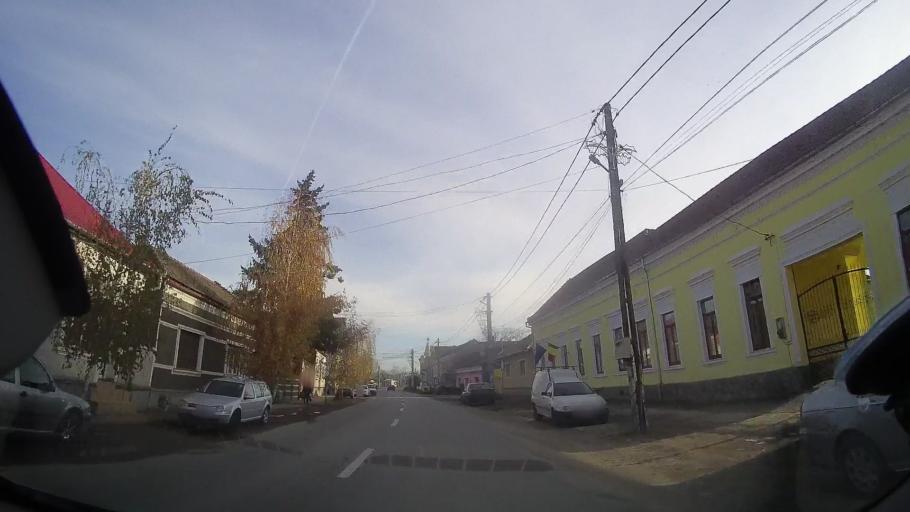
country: RO
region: Bihor
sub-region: Comuna Tileagd
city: Tileagd
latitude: 47.0720
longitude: 22.1979
